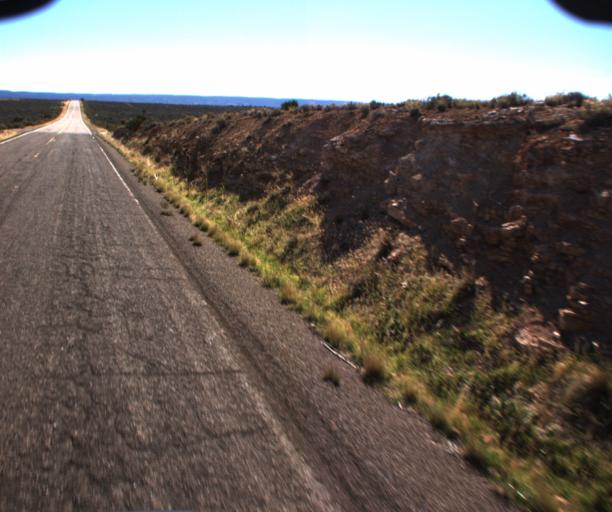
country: US
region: Arizona
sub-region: Coconino County
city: Fredonia
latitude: 36.8955
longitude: -112.3649
